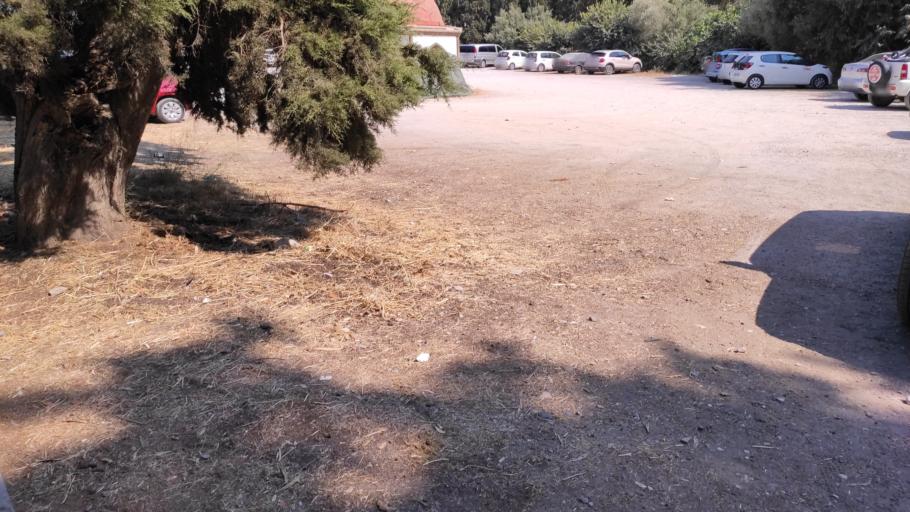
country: GR
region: South Aegean
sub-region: Nomos Dodekanisou
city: Kos
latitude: 36.8902
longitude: 27.2852
